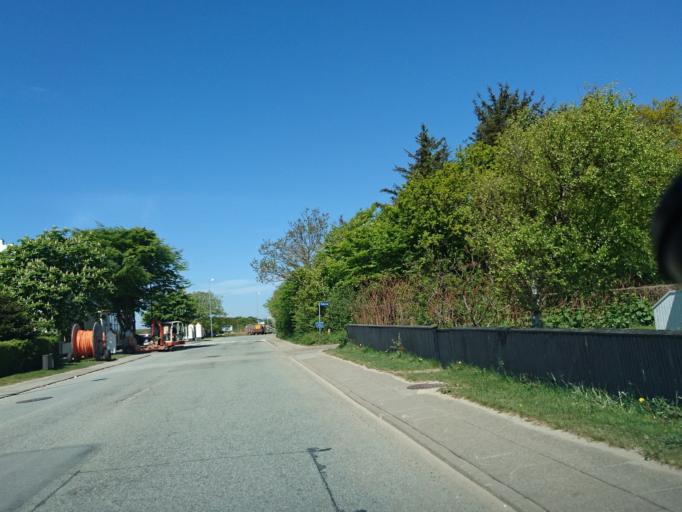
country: DK
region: North Denmark
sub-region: Hjorring Kommune
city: Sindal
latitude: 57.5927
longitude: 10.1852
